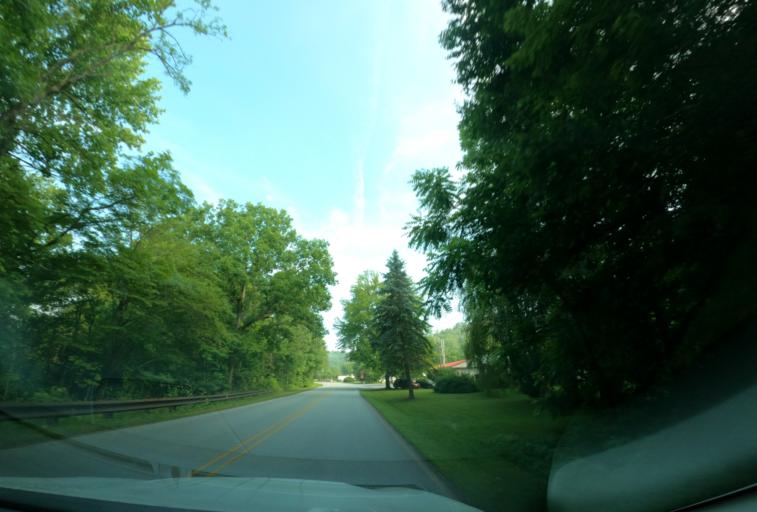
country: US
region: North Carolina
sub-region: Transylvania County
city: Brevard
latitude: 35.2265
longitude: -82.8702
